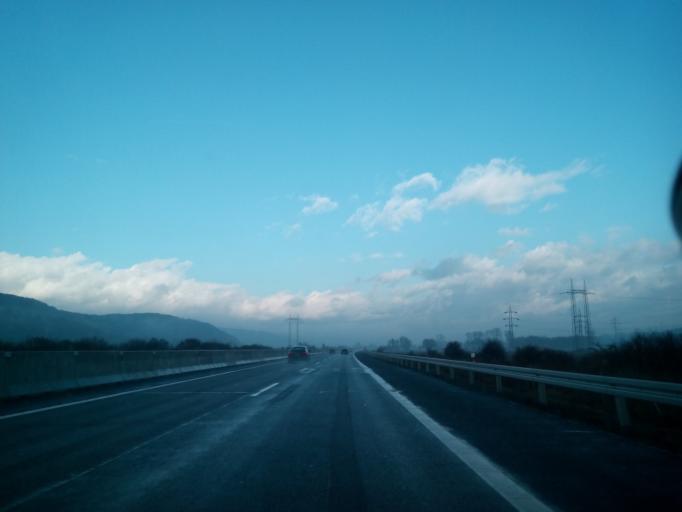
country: SK
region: Presovsky
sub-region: Okres Presov
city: Presov
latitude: 48.8822
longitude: 21.2506
